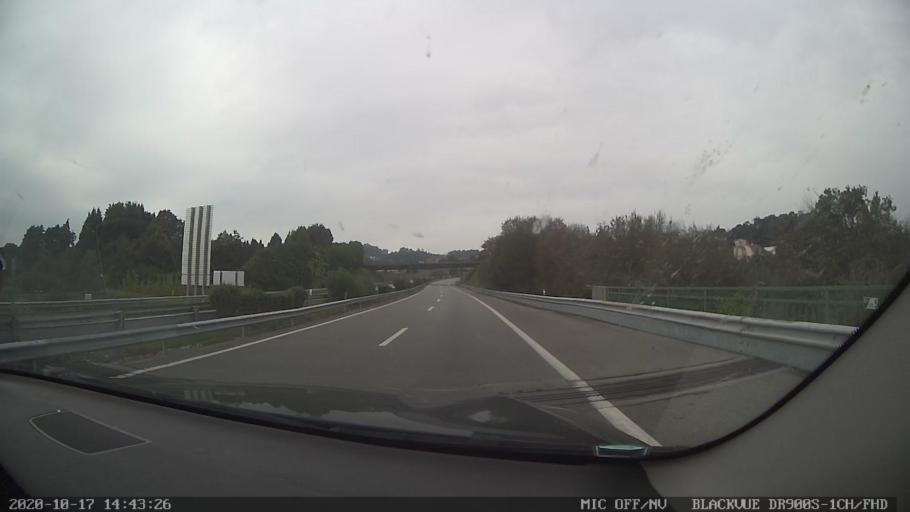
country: PT
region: Braga
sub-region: Braga
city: Oliveira
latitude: 41.5152
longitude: -8.4759
